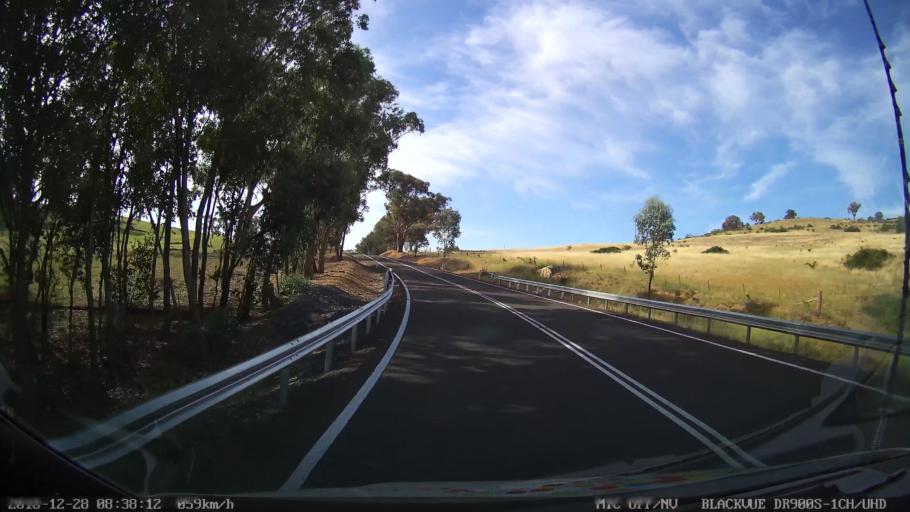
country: AU
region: New South Wales
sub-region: Blayney
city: Blayney
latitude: -34.0015
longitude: 149.3146
